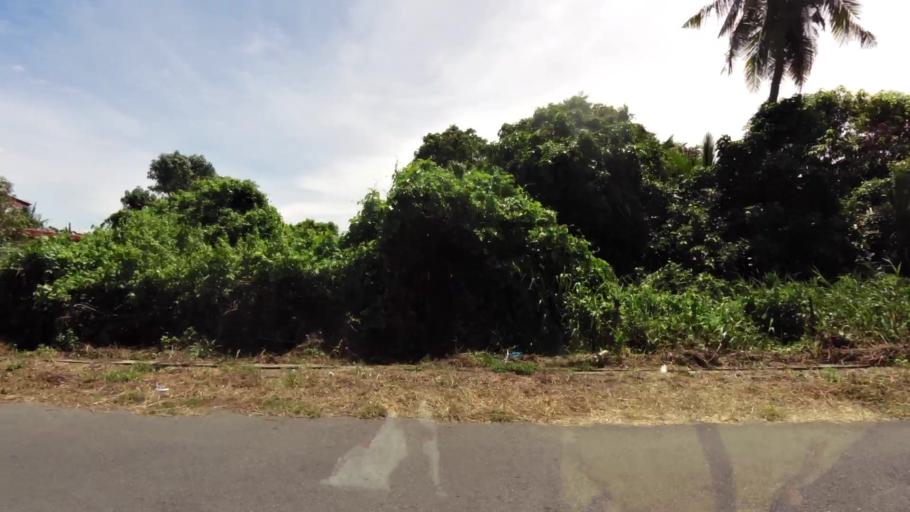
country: BN
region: Belait
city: Kuala Belait
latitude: 4.5897
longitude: 114.2224
